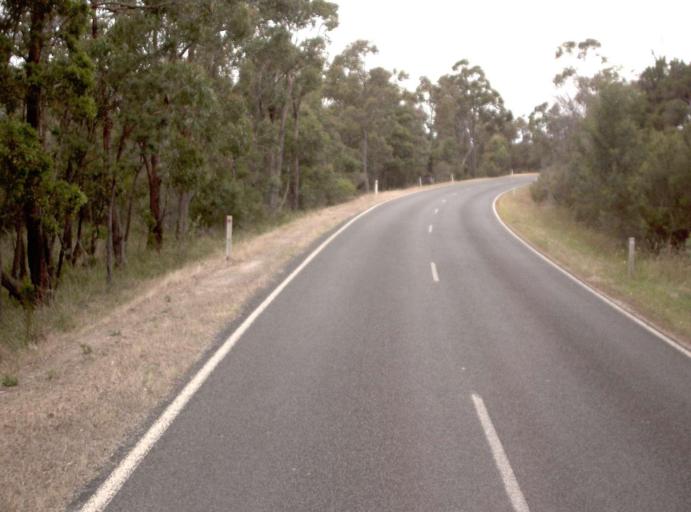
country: AU
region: Victoria
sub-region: Latrobe
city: Traralgon
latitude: -38.4977
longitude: 146.8335
